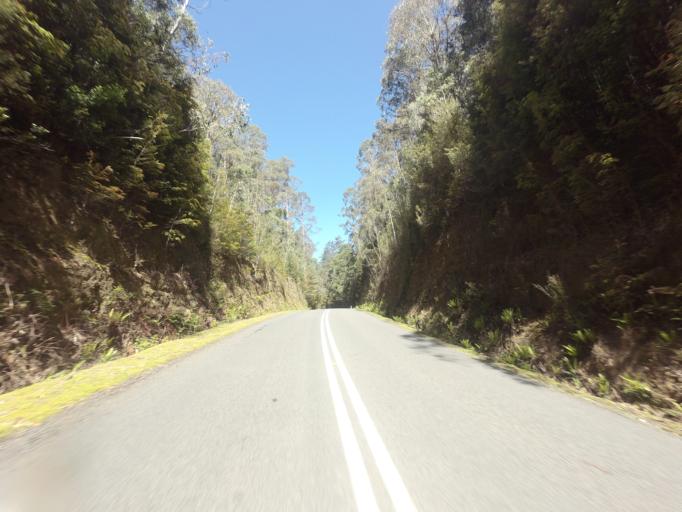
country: AU
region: Tasmania
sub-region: Huon Valley
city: Geeveston
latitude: -42.8213
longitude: 146.3110
